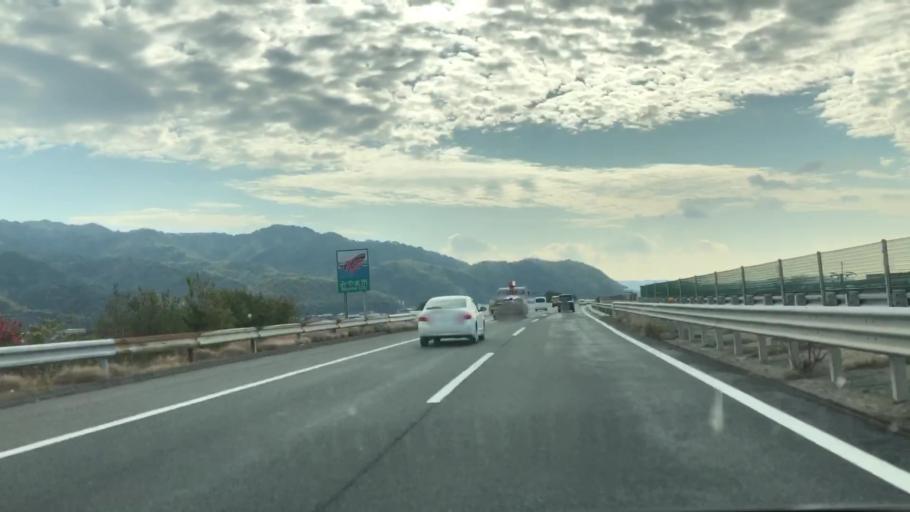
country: JP
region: Fukuoka
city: Setakamachi-takayanagi
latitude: 33.1796
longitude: 130.5176
